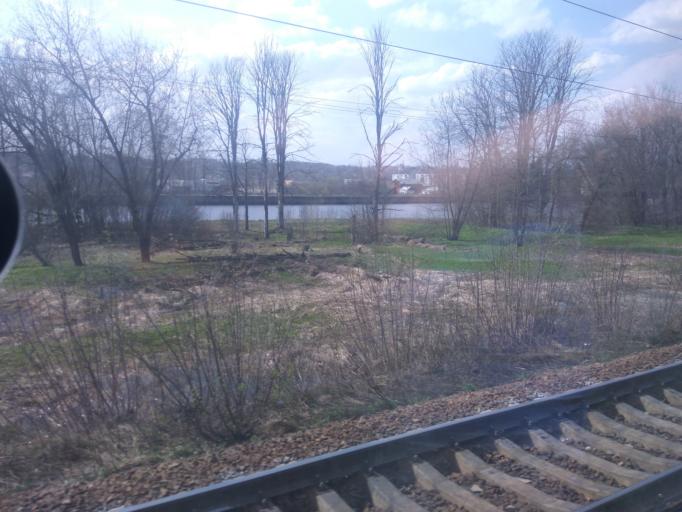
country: RU
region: Moskovskaya
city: Yakhroma
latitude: 56.2811
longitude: 37.5059
